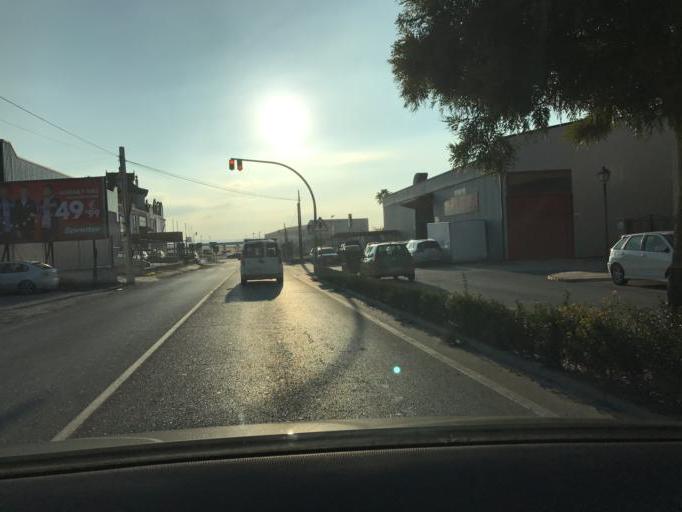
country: ES
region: Andalusia
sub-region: Provincia de Granada
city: Atarfe
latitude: 37.2163
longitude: -3.6889
